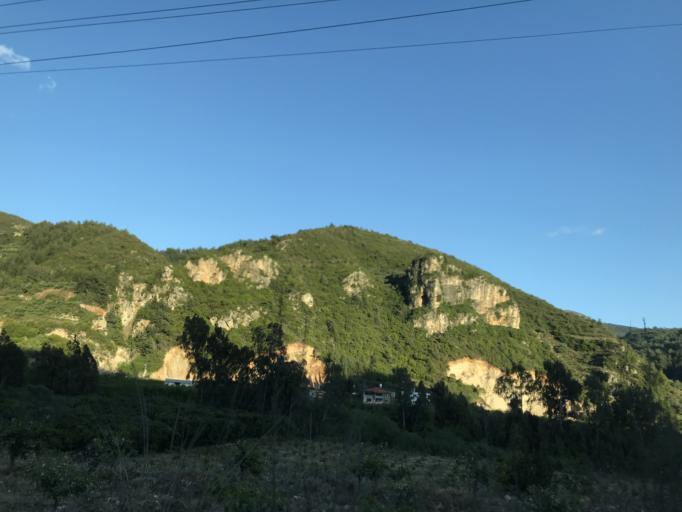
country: TR
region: Hatay
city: Buyukcat
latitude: 36.0799
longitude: 36.0462
